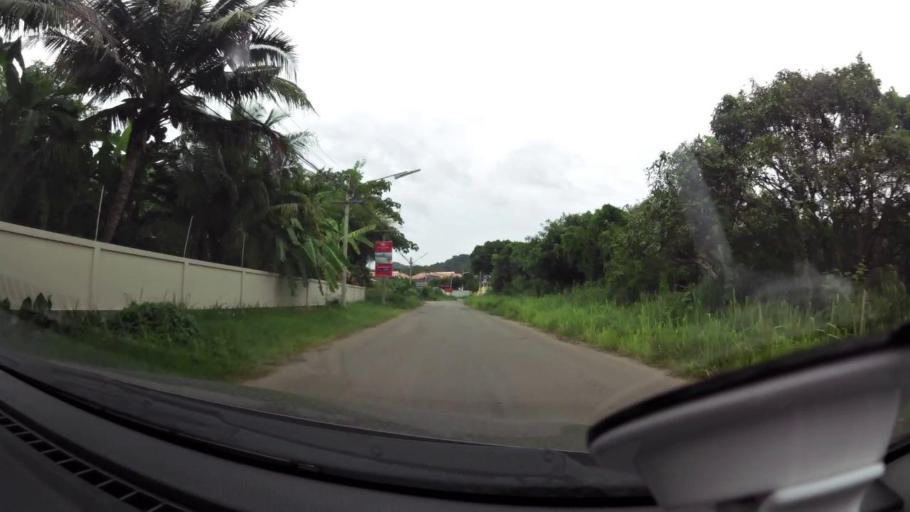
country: TH
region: Prachuap Khiri Khan
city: Pran Buri
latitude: 12.4471
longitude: 99.9711
